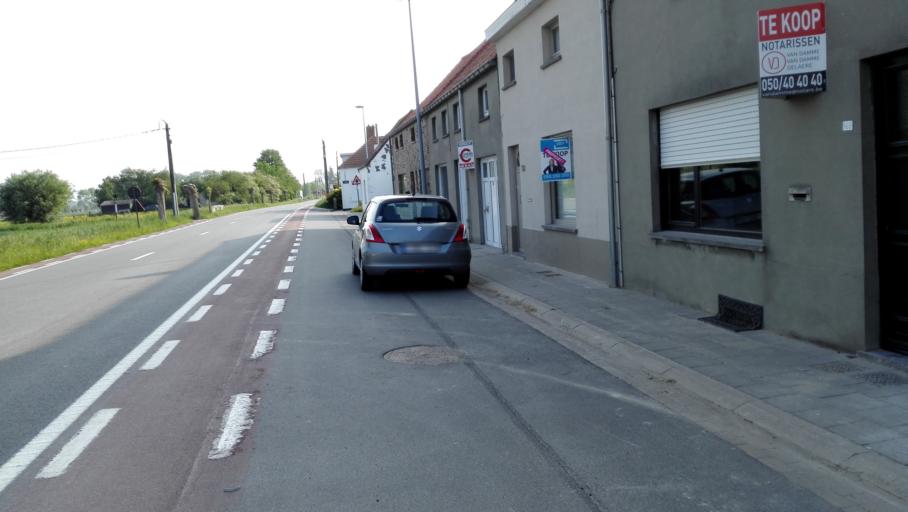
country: BE
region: Flanders
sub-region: Provincie West-Vlaanderen
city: Zuienkerke
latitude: 51.2877
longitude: 3.1758
